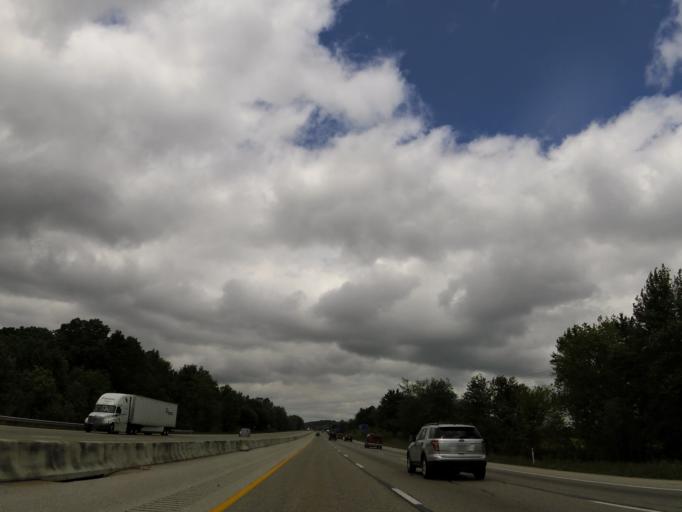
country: US
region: Kentucky
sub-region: Laurel County
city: London
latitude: 37.0926
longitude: -84.1002
